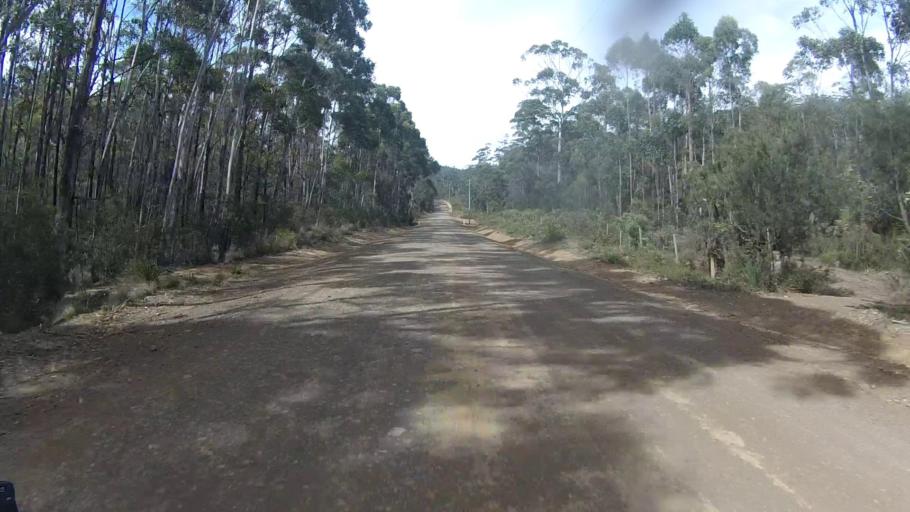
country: AU
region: Tasmania
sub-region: Sorell
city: Sorell
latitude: -42.6793
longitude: 147.8825
